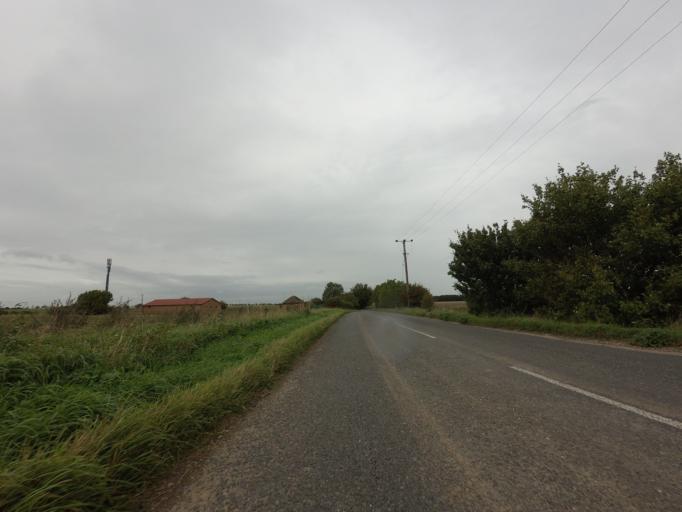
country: GB
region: England
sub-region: Cambridgeshire
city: Harston
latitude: 52.0807
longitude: 0.0823
